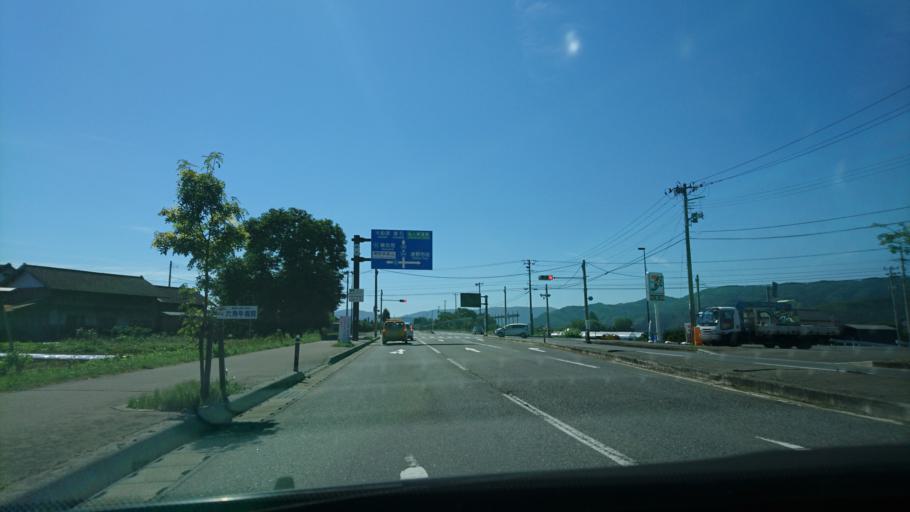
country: JP
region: Iwate
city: Tono
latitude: 39.3259
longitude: 141.5642
